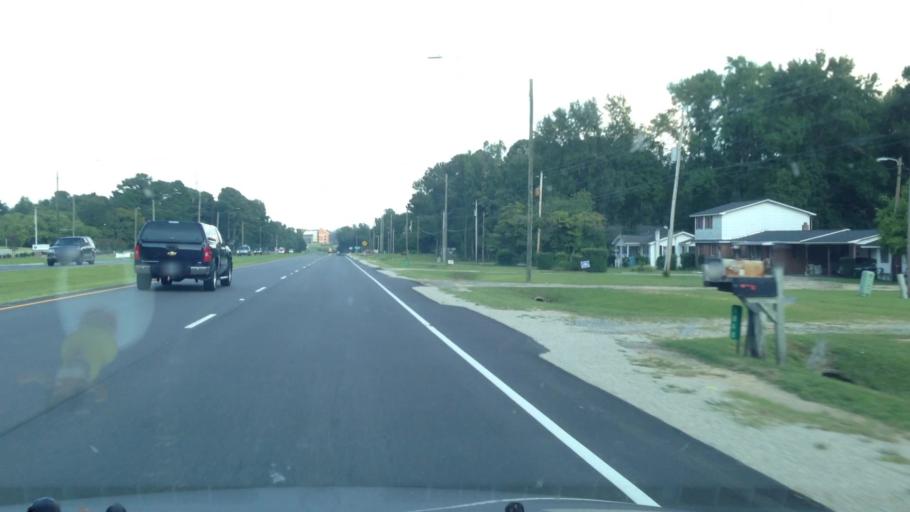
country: US
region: North Carolina
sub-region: Harnett County
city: Buies Creek
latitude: 35.4087
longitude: -78.7727
